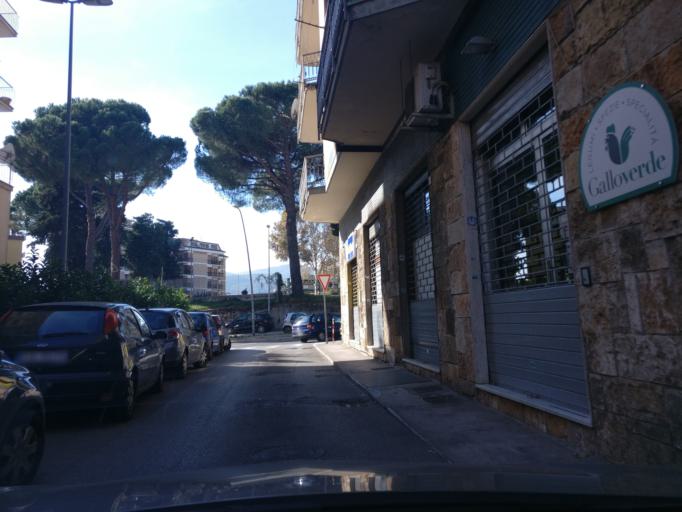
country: IT
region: Campania
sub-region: Provincia di Avellino
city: Avellino
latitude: 40.9208
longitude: 14.7835
